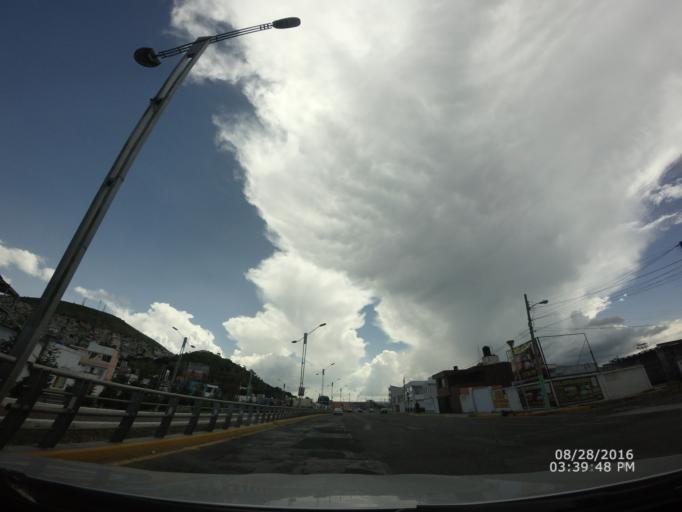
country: MX
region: Hidalgo
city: Pachuca de Soto
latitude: 20.1167
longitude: -98.7365
